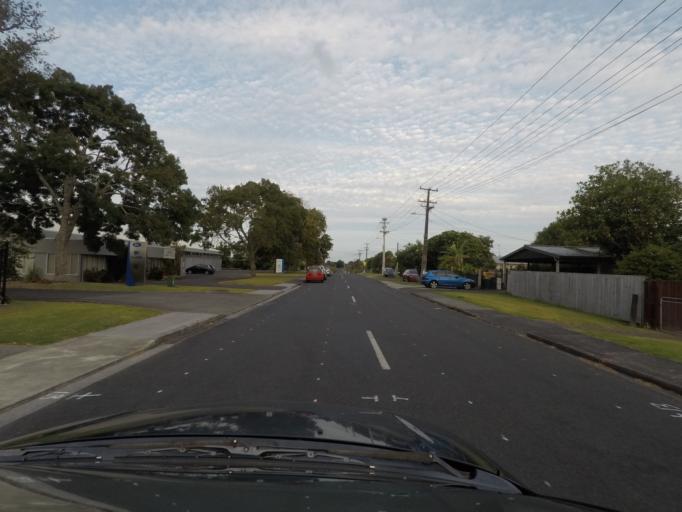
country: NZ
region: Auckland
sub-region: Auckland
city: Rosebank
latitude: -36.8316
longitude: 174.6490
